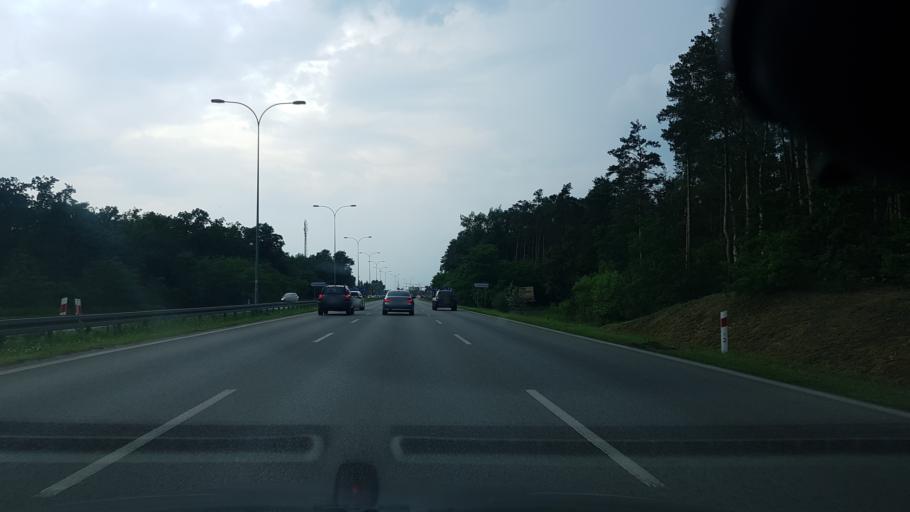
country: PL
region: Masovian Voivodeship
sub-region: Powiat legionowski
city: Jablonna
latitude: 52.3595
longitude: 20.9384
